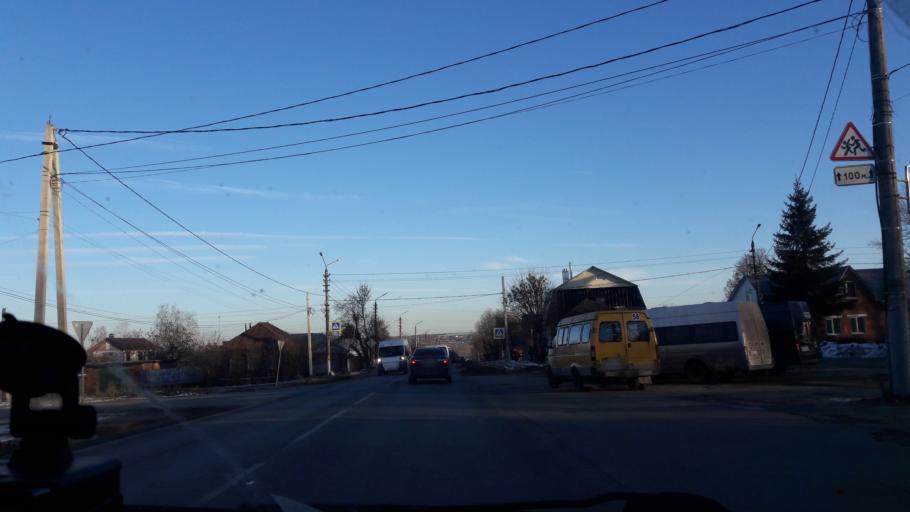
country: RU
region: Tula
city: Gorelki
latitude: 54.2411
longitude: 37.6271
